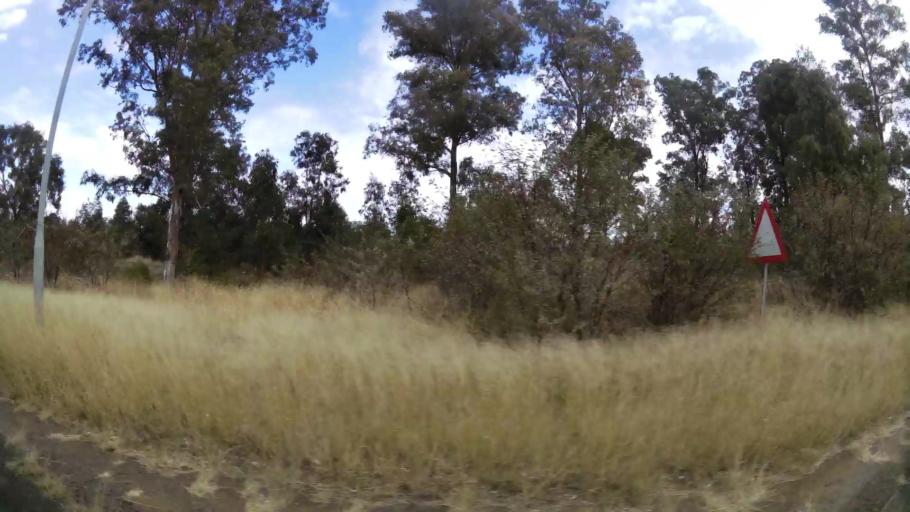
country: ZA
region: Orange Free State
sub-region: Fezile Dabi District Municipality
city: Kroonstad
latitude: -27.6329
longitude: 27.2173
